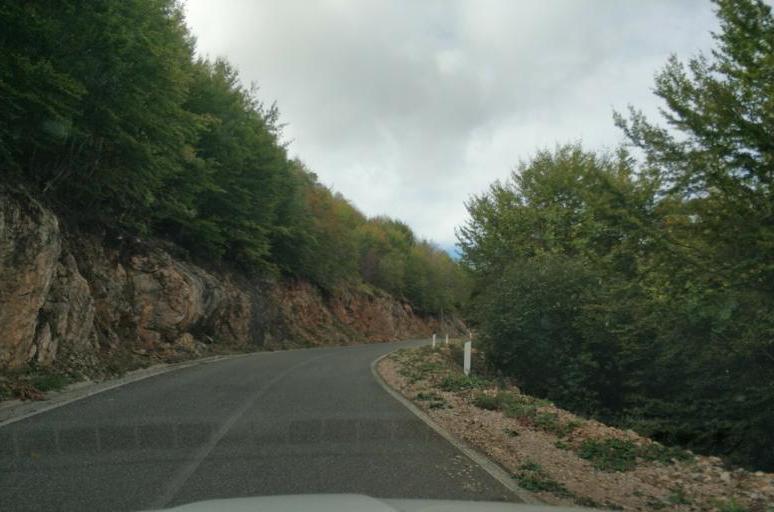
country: AL
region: Durres
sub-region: Rrethi i Krujes
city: Kruje
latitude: 41.5225
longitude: 19.8067
